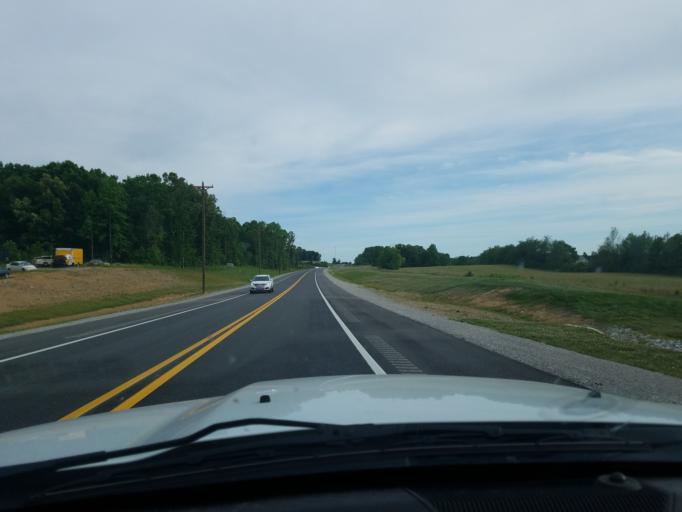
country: US
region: Tennessee
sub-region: Putnam County
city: Cookeville
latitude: 36.1750
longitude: -85.5615
